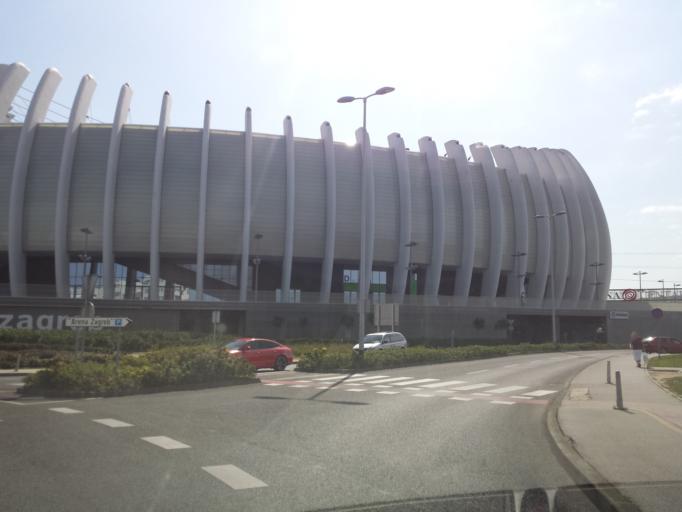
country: HR
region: Grad Zagreb
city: Novi Zagreb
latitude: 45.7727
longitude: 15.9439
